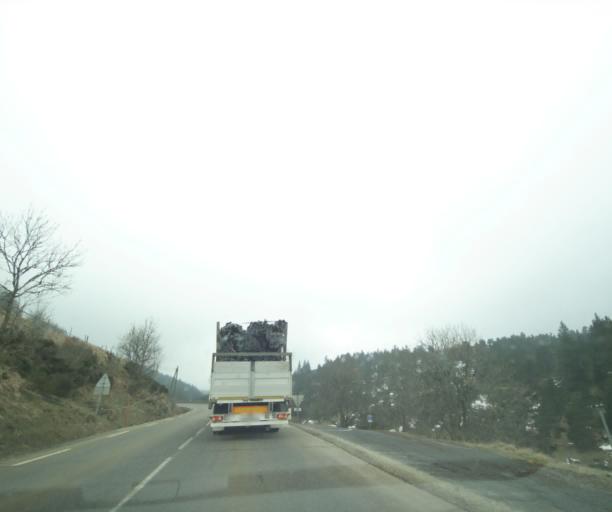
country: FR
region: Languedoc-Roussillon
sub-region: Departement de la Lozere
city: Langogne
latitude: 44.7232
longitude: 4.0048
